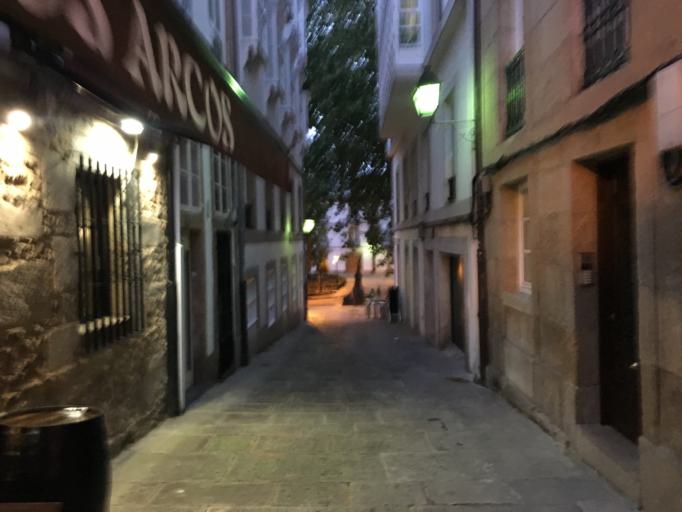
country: ES
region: Galicia
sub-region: Provincia da Coruna
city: A Coruna
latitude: 43.3704
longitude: -8.3929
